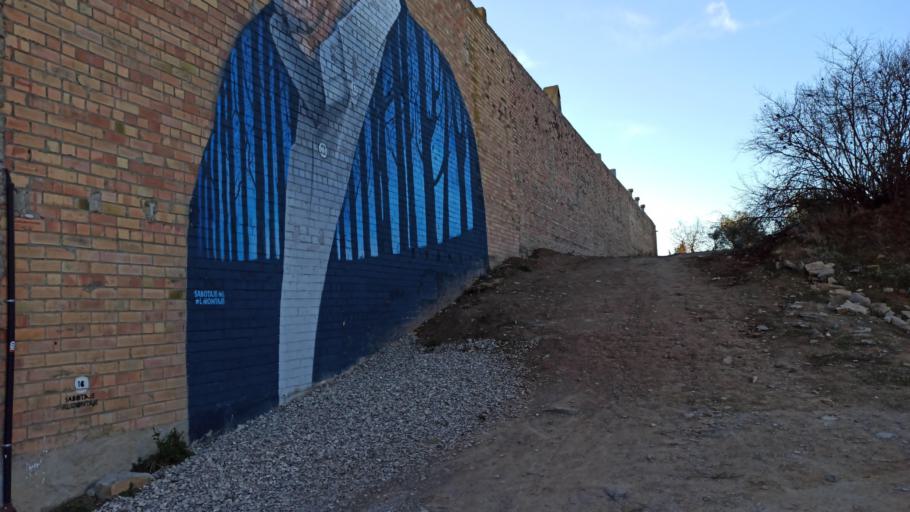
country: ES
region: Catalonia
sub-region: Provincia de Lleida
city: Penelles
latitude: 41.7596
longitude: 0.9667
